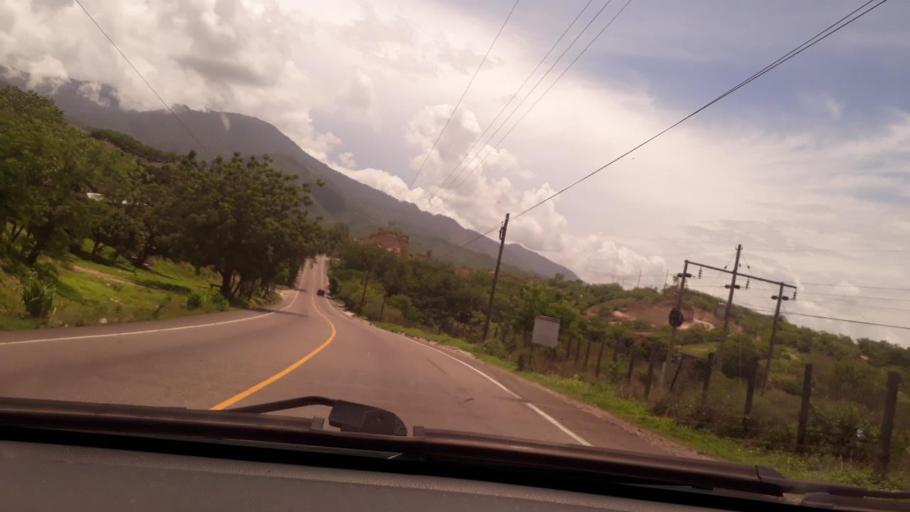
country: GT
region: Zacapa
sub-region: Municipio de Zacapa
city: Gualan
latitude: 15.0952
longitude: -89.4310
